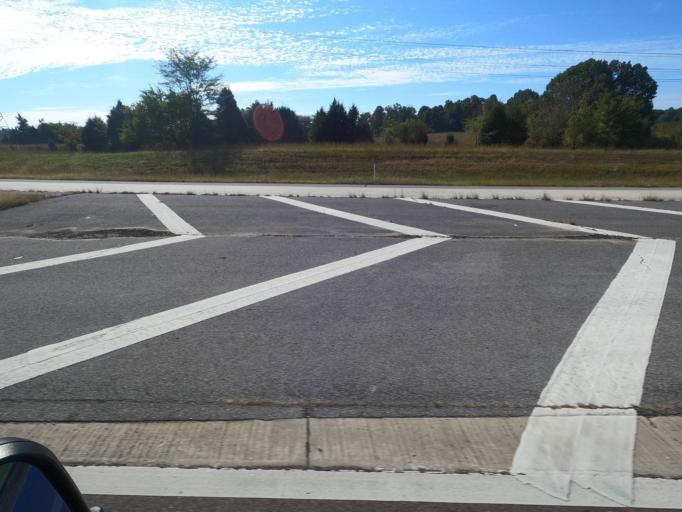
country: US
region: Tennessee
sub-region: Shelby County
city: Arlington
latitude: 35.3113
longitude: -89.7322
